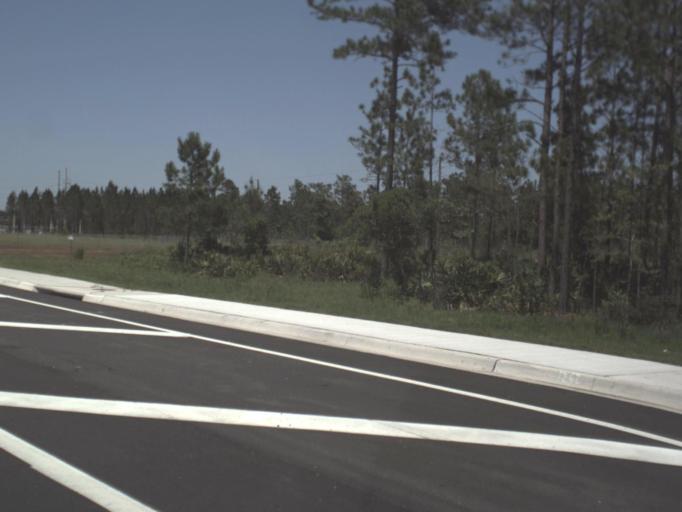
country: US
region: Florida
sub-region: Clay County
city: Lakeside
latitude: 30.1589
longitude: -81.8307
